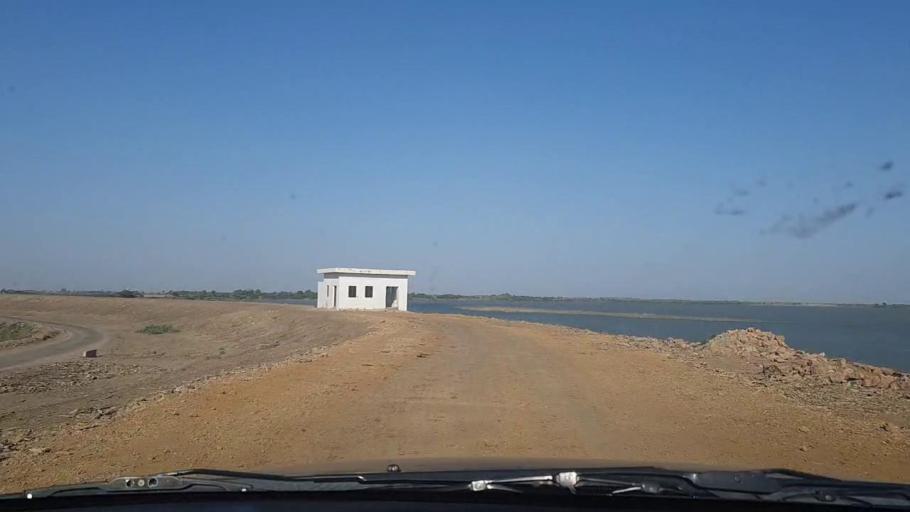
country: PK
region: Sindh
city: Chuhar Jamali
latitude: 24.3572
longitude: 67.7622
